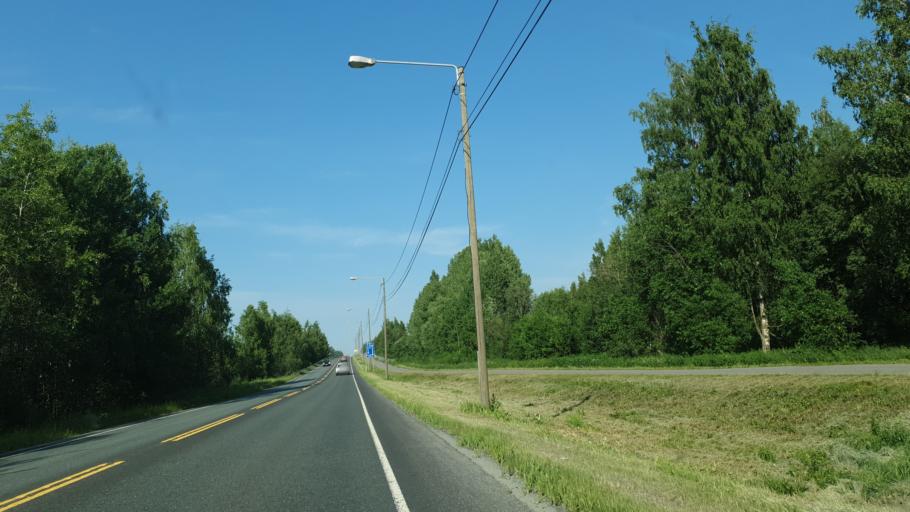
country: FI
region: Northern Savo
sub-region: Kuopio
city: Siilinjaervi
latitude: 63.0947
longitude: 27.7271
